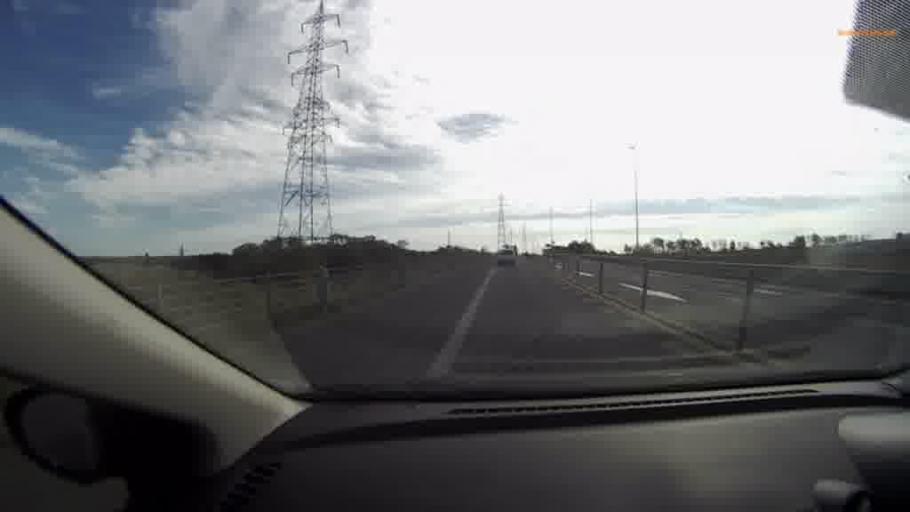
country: JP
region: Hokkaido
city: Kushiro
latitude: 43.0310
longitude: 144.3999
